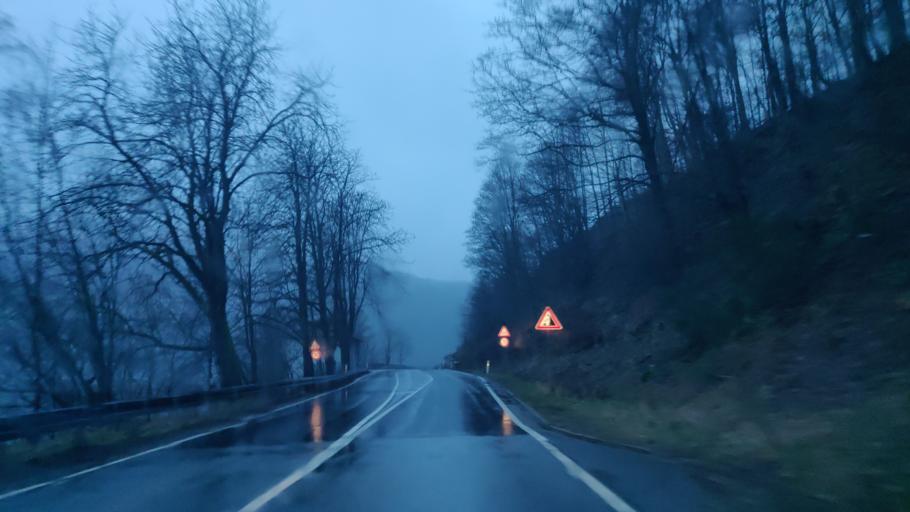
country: DE
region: Lower Saxony
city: Bad Lauterberg im Harz
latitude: 51.6491
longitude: 10.5070
